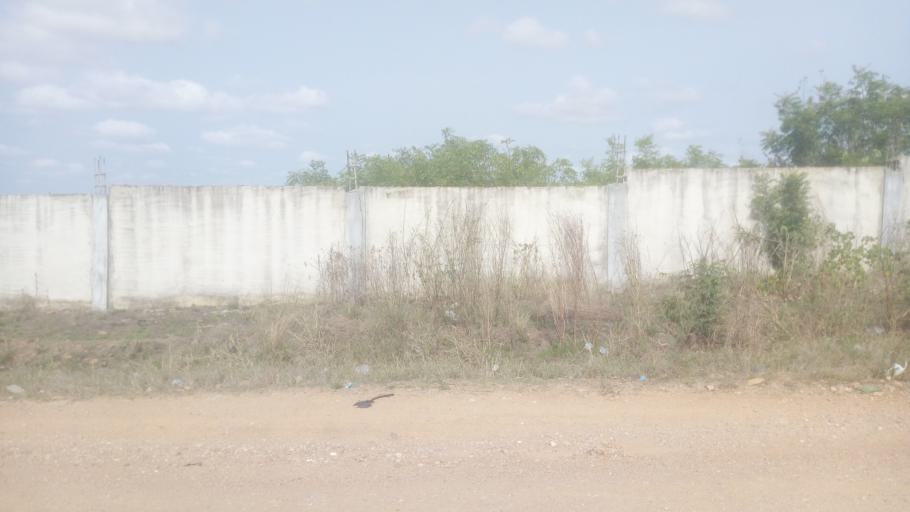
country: GH
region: Central
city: Winneba
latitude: 5.3784
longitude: -0.6287
